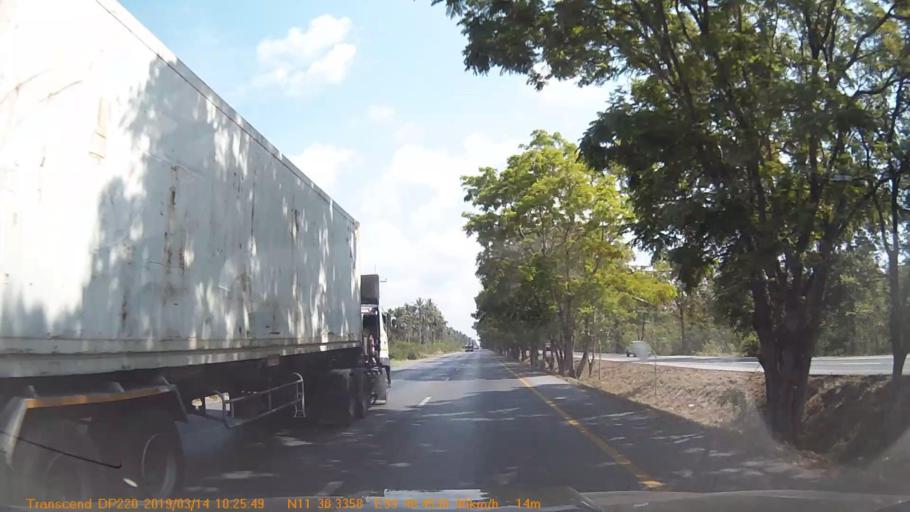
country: TH
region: Prachuap Khiri Khan
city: Thap Sakae
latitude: 11.6314
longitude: 99.6716
